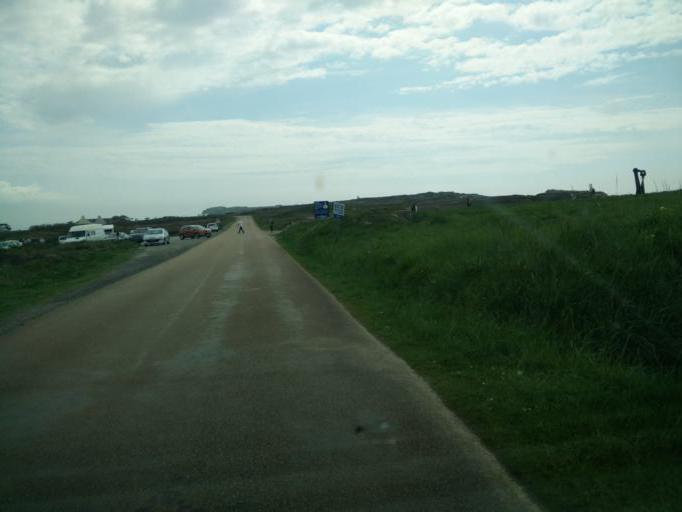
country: FR
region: Brittany
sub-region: Departement du Finistere
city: Camaret-sur-Mer
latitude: 48.2684
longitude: -4.6148
